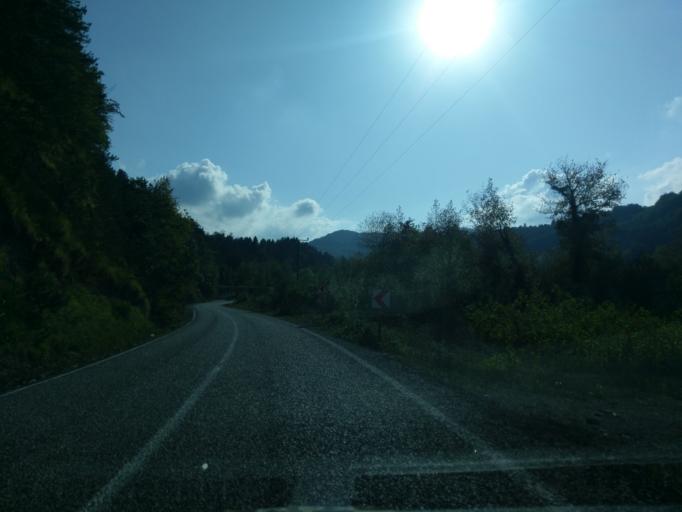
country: TR
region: Sinop
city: Yenikonak
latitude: 41.8793
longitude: 34.5561
